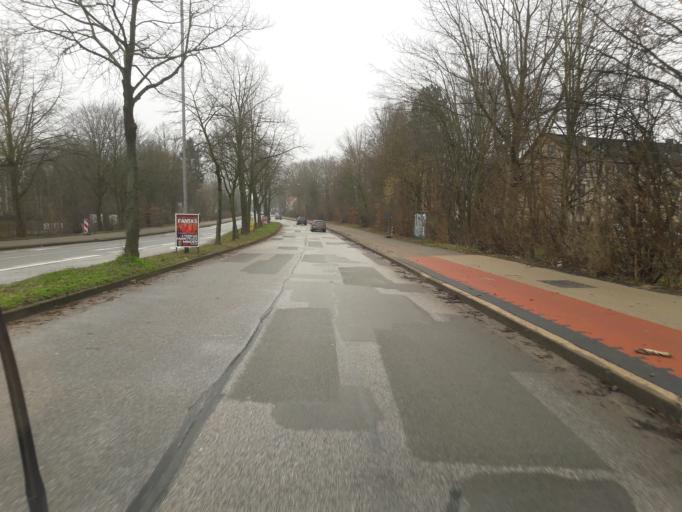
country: DE
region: North Rhine-Westphalia
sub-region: Regierungsbezirk Detmold
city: Minden
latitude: 52.3007
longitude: 8.8933
